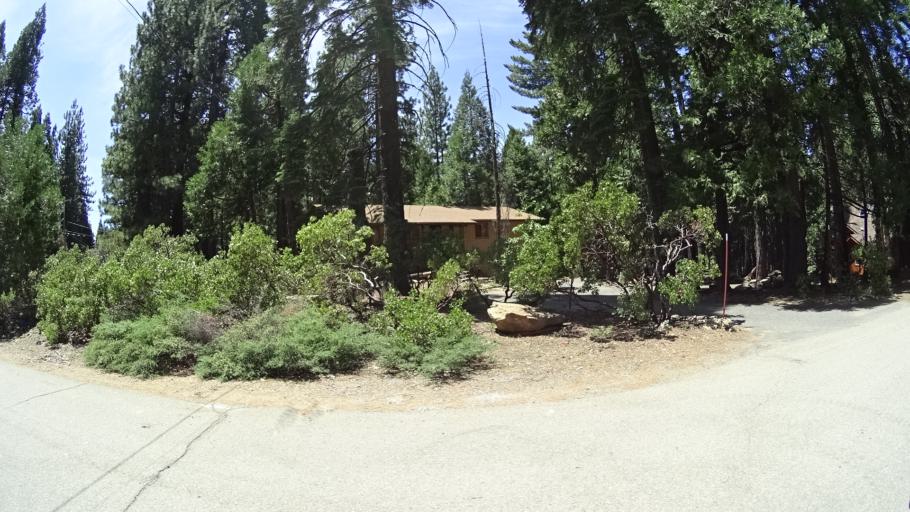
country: US
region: California
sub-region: Calaveras County
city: Arnold
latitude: 38.3015
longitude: -120.2697
